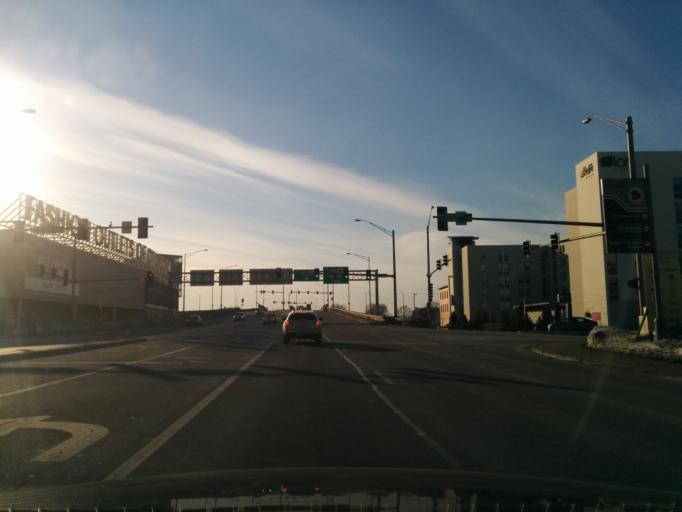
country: US
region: Illinois
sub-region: Cook County
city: Schiller Park
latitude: 41.9769
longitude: -87.8658
